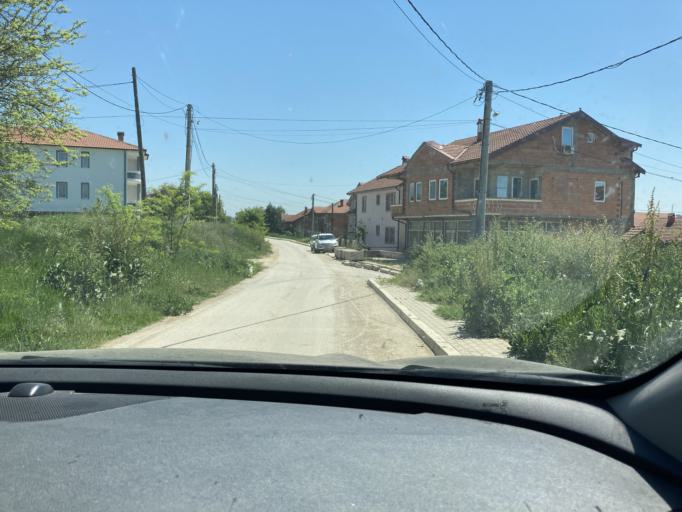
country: MK
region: Suto Orizari
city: Suto Orizare
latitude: 42.0396
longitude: 21.4036
